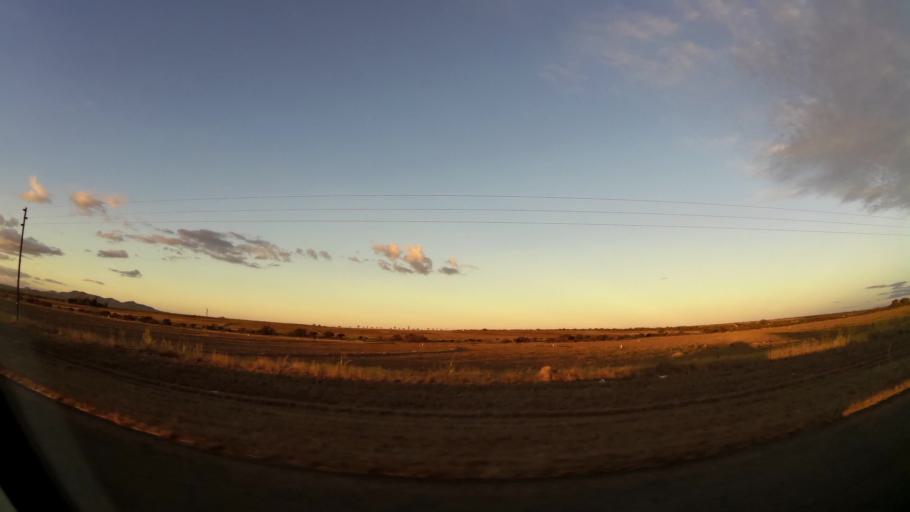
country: ZA
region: Limpopo
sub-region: Capricorn District Municipality
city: Polokwane
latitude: -23.7884
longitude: 29.4760
